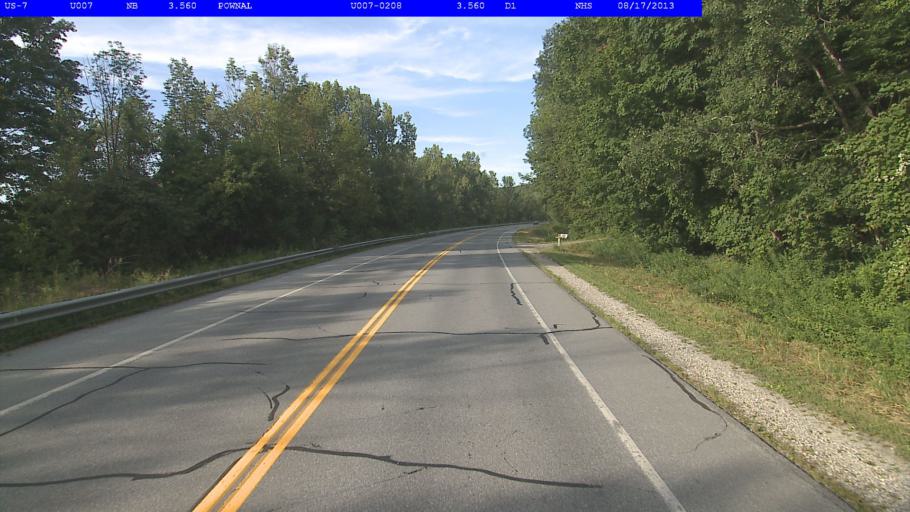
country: US
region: Massachusetts
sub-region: Berkshire County
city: Williamstown
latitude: 42.7861
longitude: -73.2414
